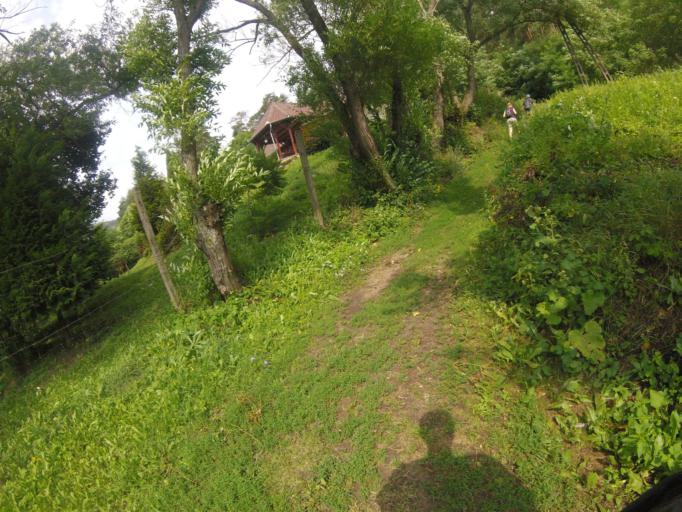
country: HU
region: Borsod-Abauj-Zemplen
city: Sarospatak
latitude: 48.4478
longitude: 21.5255
